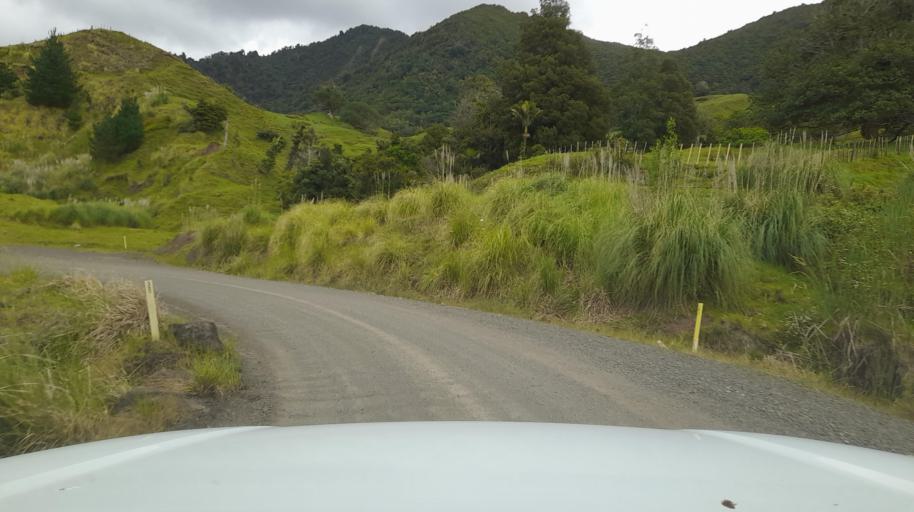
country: NZ
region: Northland
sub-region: Far North District
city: Kaitaia
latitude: -35.3360
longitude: 173.3552
